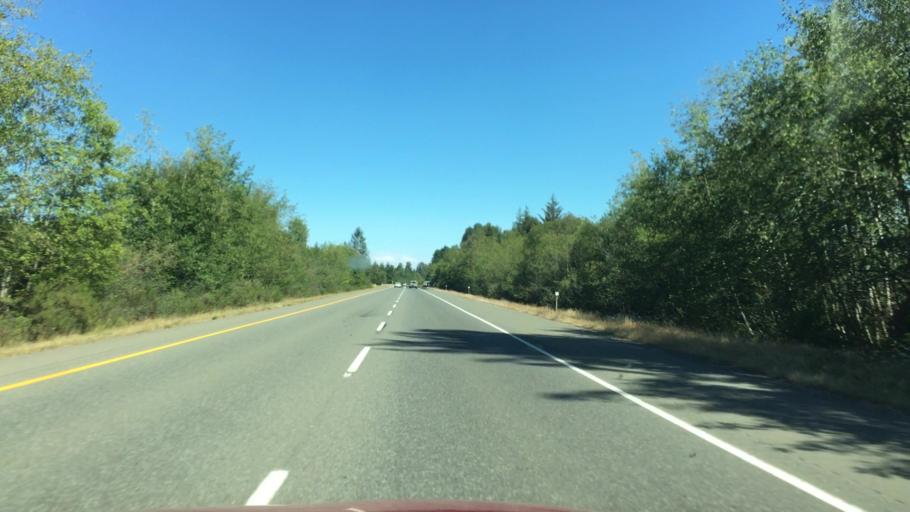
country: CA
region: British Columbia
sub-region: Regional District of Nanaimo
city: Parksville
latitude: 49.3167
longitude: -124.3797
